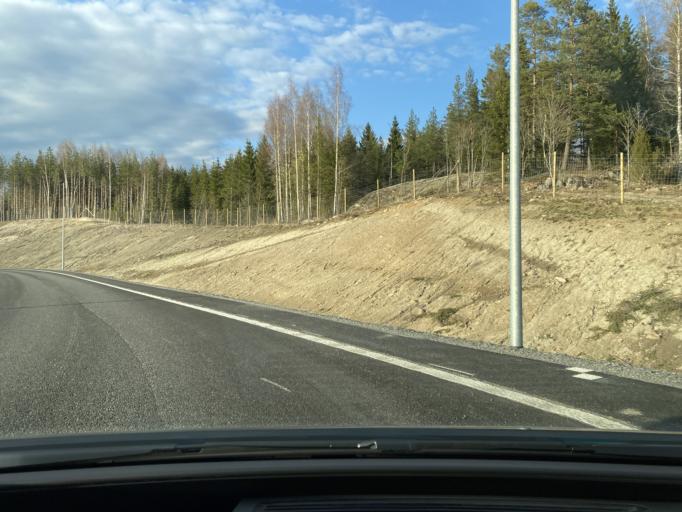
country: FI
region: Uusimaa
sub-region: Helsinki
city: Nurmijaervi
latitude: 60.3855
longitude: 24.8182
